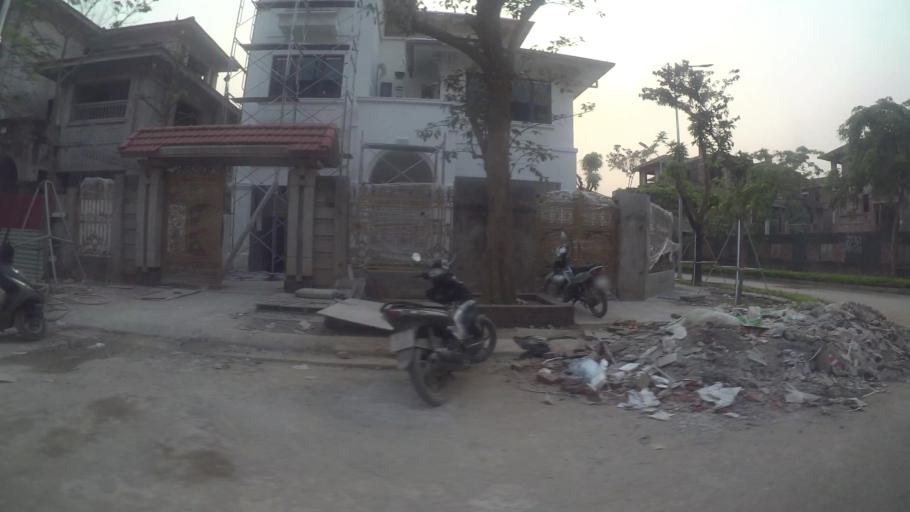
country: VN
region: Ha Noi
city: Cau Dien
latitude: 21.0011
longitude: 105.7295
